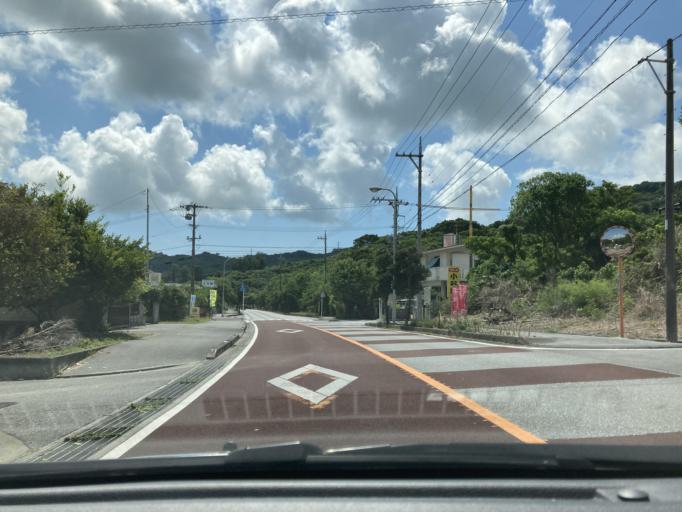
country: JP
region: Okinawa
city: Tomigusuku
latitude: 26.1759
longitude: 127.7674
